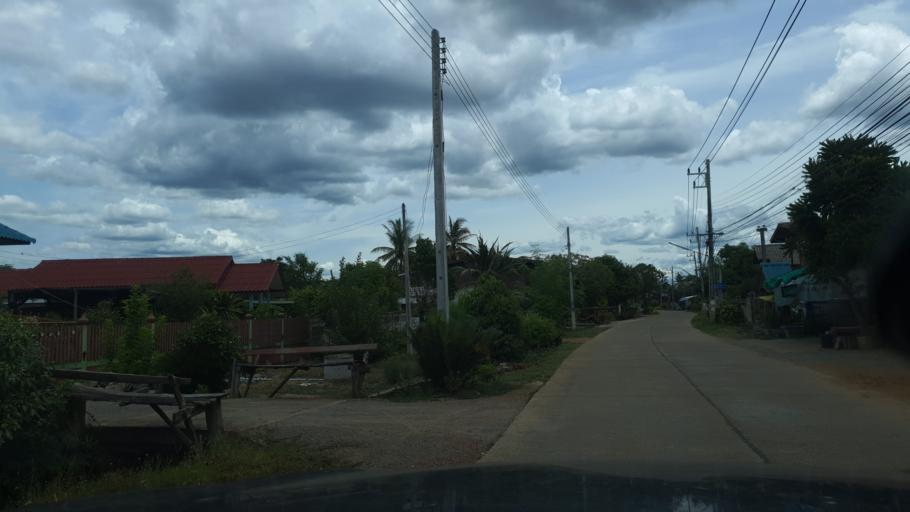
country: TH
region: Sukhothai
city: Thung Saliam
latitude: 17.3132
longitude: 99.5615
